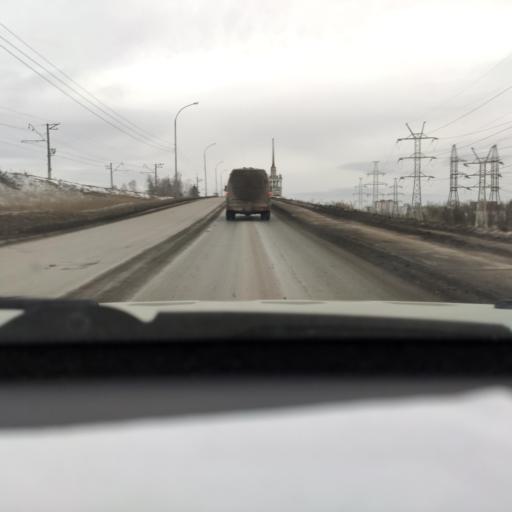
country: RU
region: Perm
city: Perm
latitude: 58.1150
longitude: 56.3375
